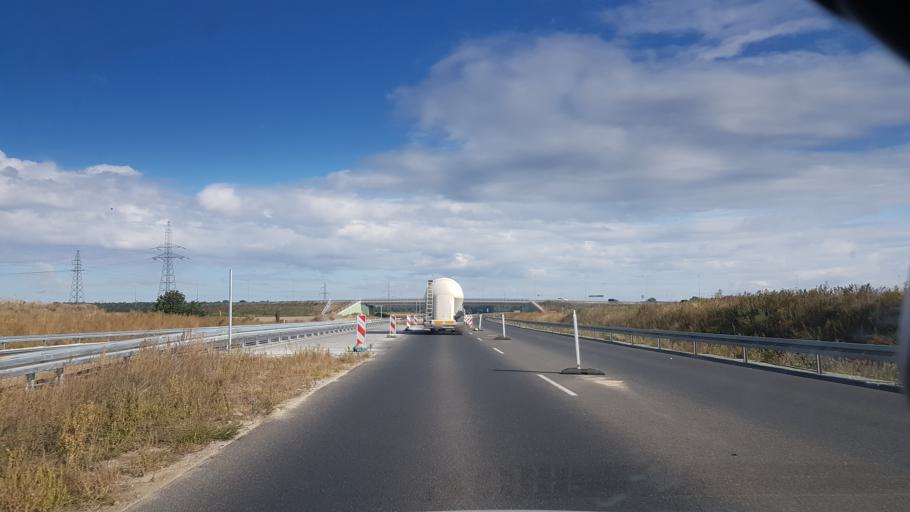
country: PL
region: Greater Poland Voivodeship
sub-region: Powiat poznanski
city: Steszew
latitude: 52.2840
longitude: 16.6727
